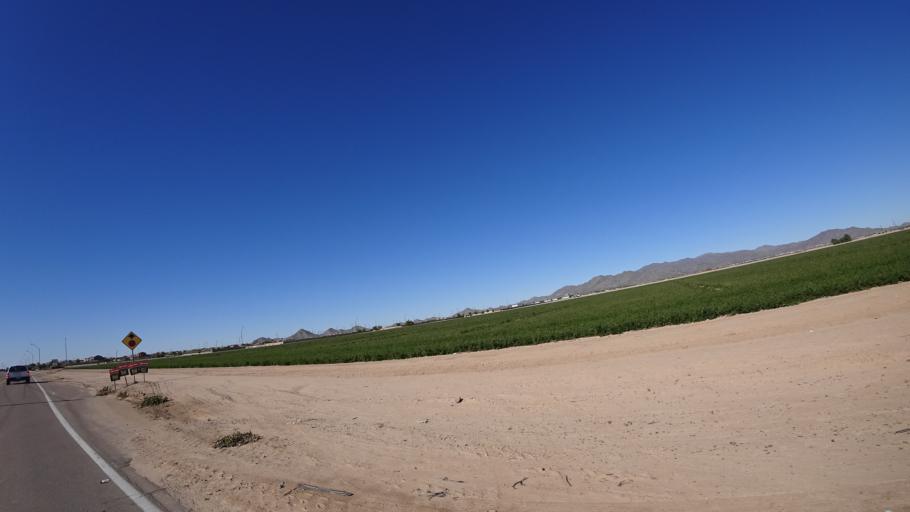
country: US
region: Arizona
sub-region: Maricopa County
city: Buckeye
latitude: 33.4066
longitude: -112.5715
